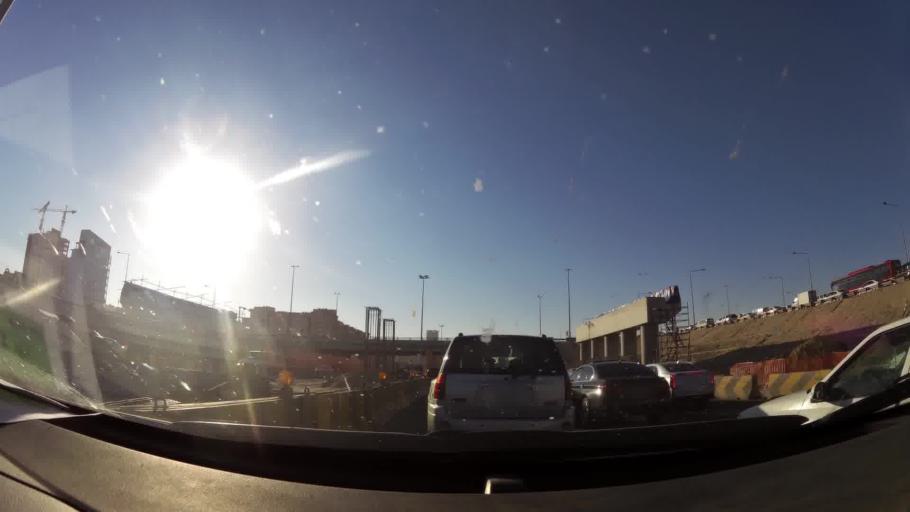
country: KW
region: Al Ahmadi
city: Al Fintas
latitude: 29.1850
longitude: 48.1116
